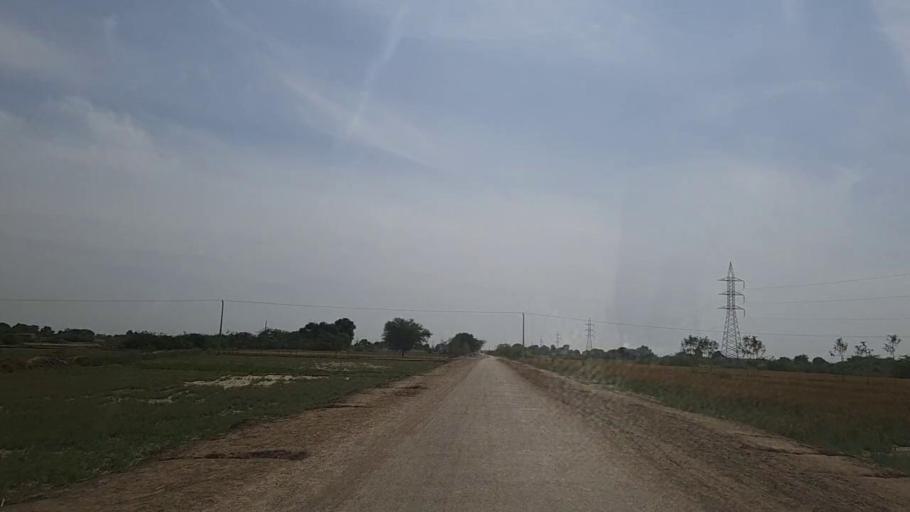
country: PK
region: Sindh
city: Kunri
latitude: 25.1867
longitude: 69.4598
